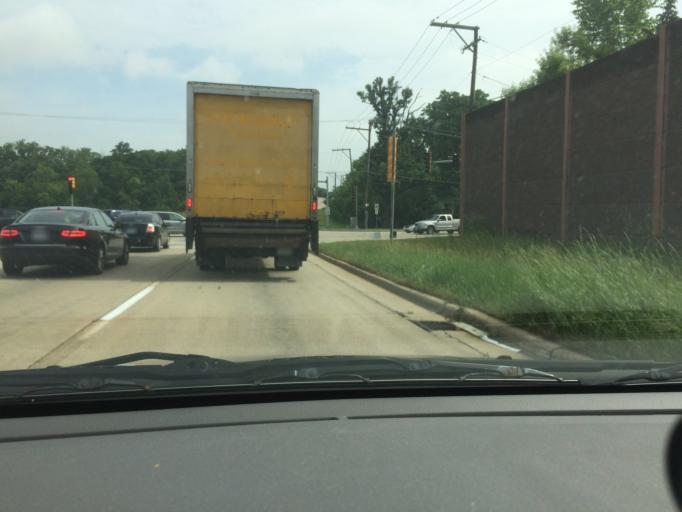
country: US
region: Illinois
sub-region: Cook County
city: Bartlett
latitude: 41.9941
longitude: -88.2072
